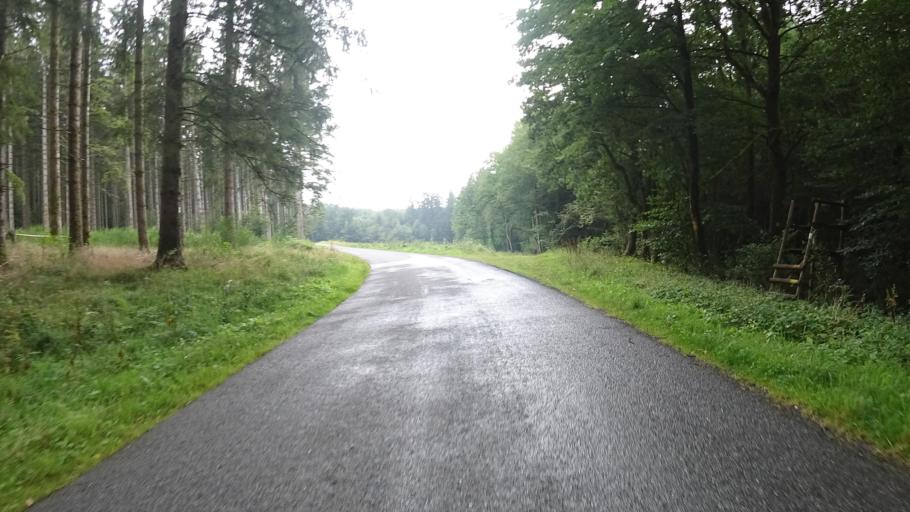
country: BE
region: Wallonia
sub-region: Province du Luxembourg
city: Chiny
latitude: 49.7818
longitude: 5.3693
